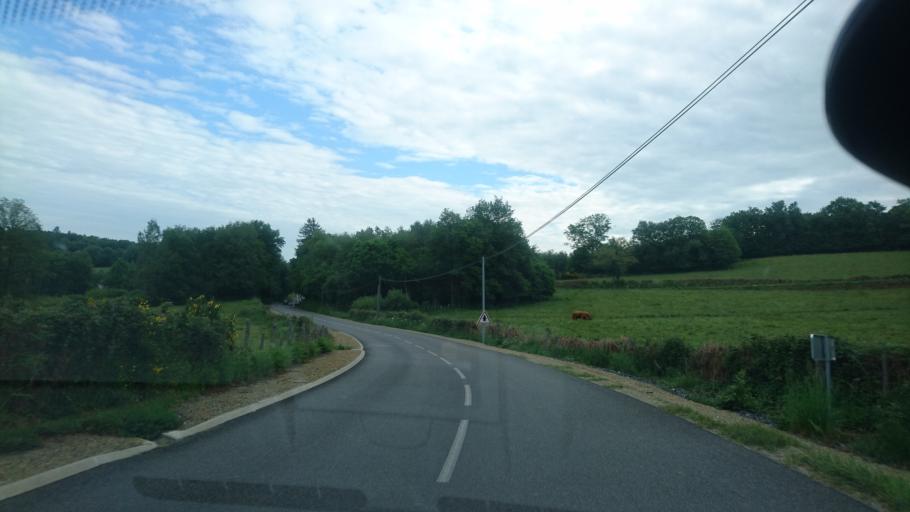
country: FR
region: Limousin
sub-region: Departement de la Haute-Vienne
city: Linards
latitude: 45.6655
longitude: 1.5664
